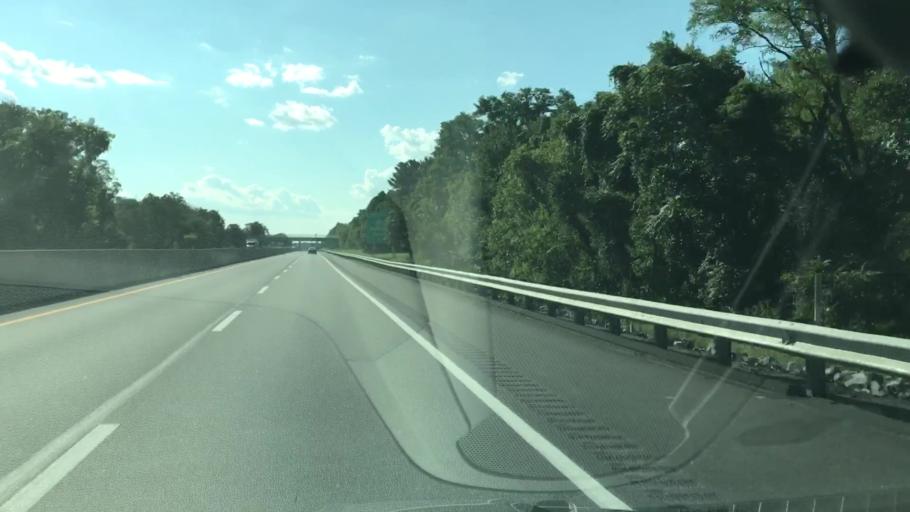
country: US
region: Pennsylvania
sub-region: Dauphin County
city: Highspire
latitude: 40.2126
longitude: -76.7657
